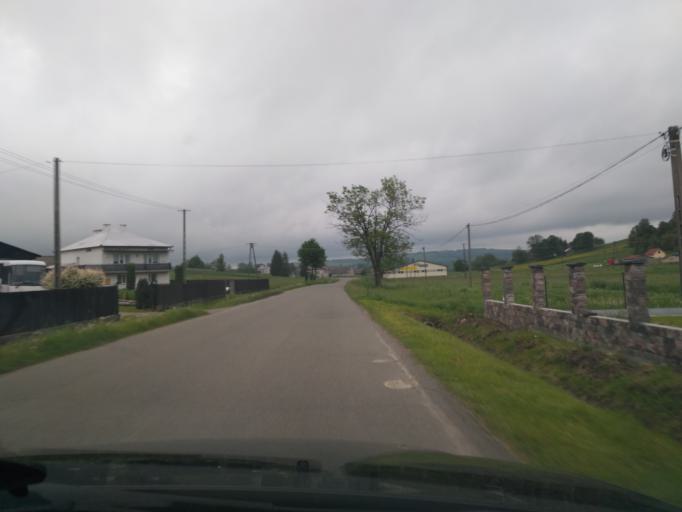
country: PL
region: Subcarpathian Voivodeship
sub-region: Powiat ropczycko-sedziszowski
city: Niedzwiada
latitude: 49.9731
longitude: 21.5350
